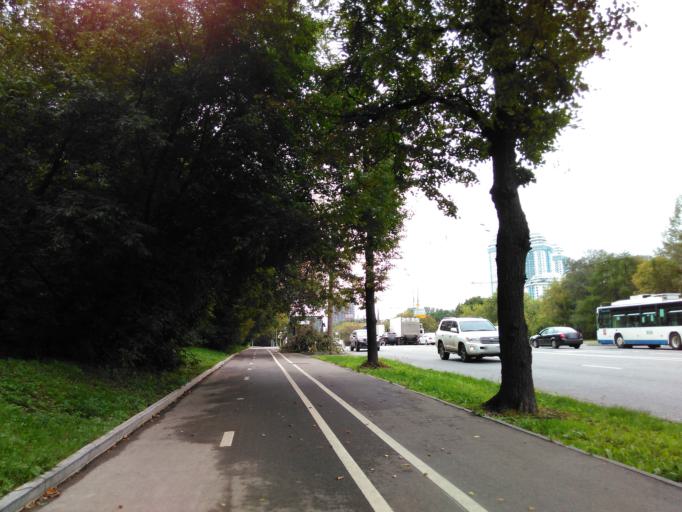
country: RU
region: Moscow
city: Vorob'yovo
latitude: 55.7172
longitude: 37.5188
